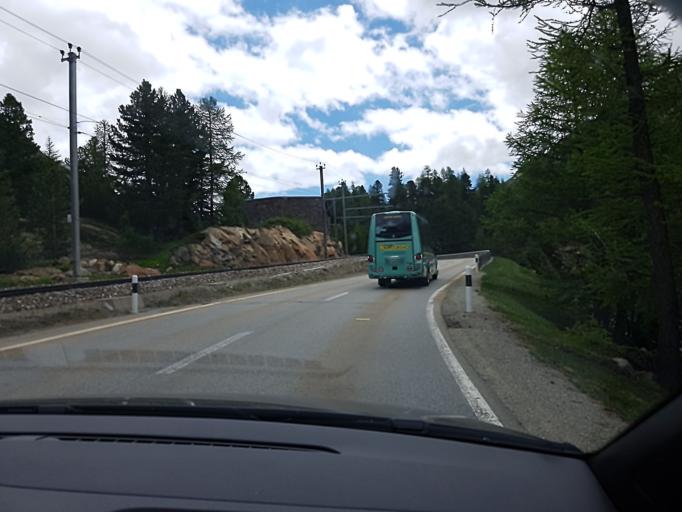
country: CH
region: Grisons
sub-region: Maloja District
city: Pontresina
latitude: 46.4530
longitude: 9.9491
